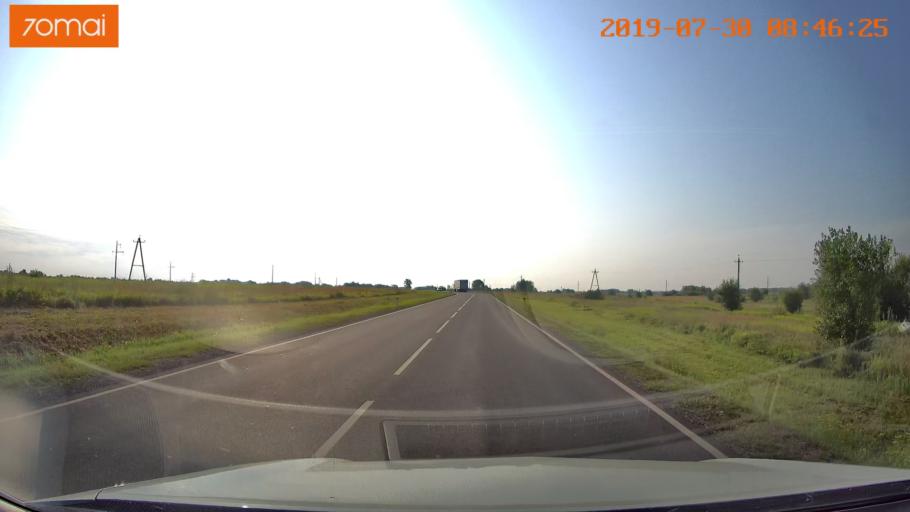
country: RU
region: Kaliningrad
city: Chernyakhovsk
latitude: 54.6234
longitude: 21.8841
